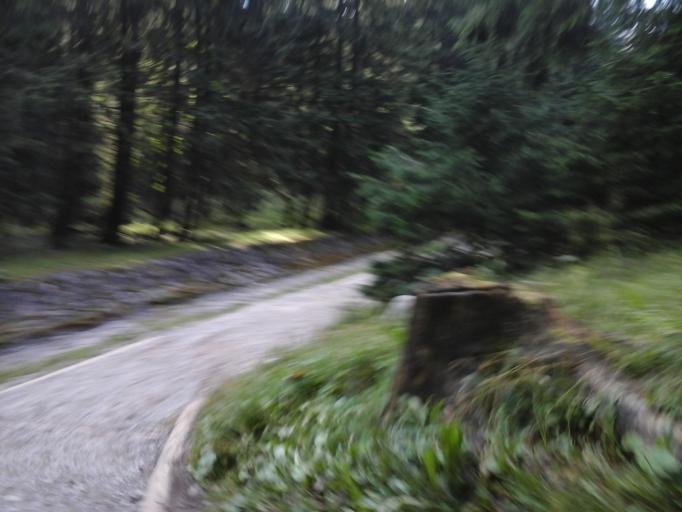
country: PL
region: Lesser Poland Voivodeship
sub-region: Powiat tatrzanski
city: Zakopane
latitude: 49.2787
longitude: 19.9815
